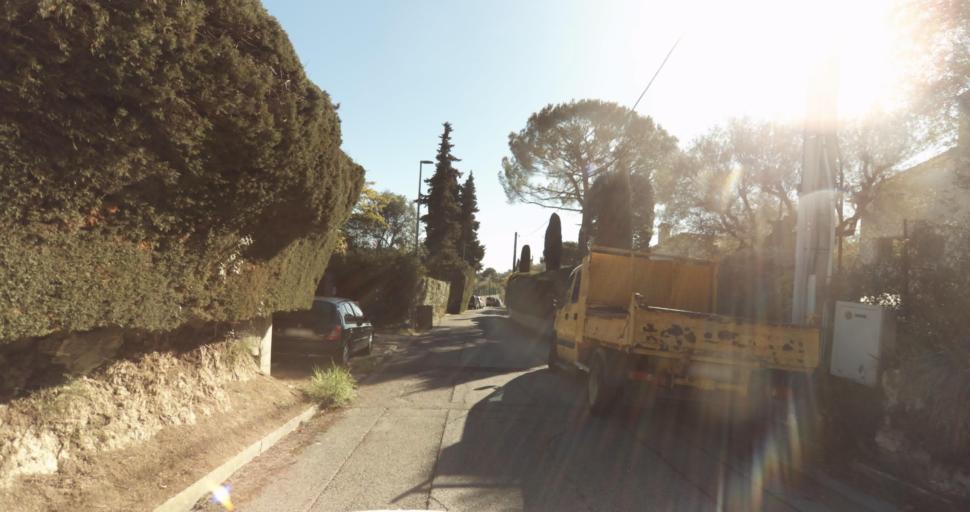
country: FR
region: Provence-Alpes-Cote d'Azur
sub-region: Departement des Alpes-Maritimes
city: Saint-Paul-de-Vence
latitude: 43.7110
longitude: 7.1290
